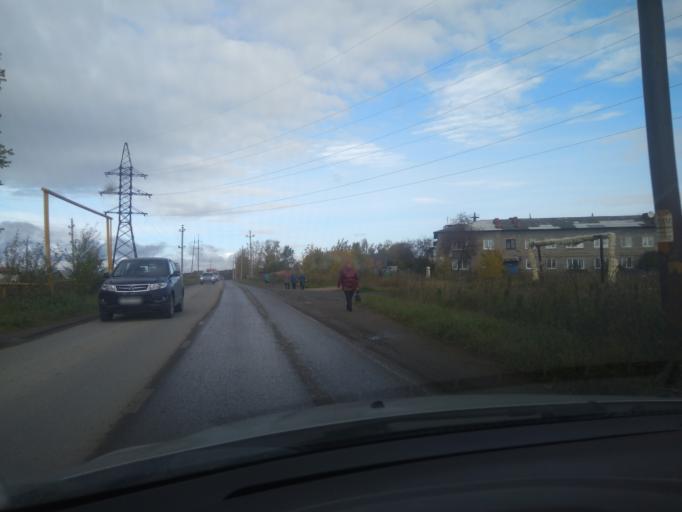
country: RU
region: Sverdlovsk
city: Nikolo-Pavlovskoye
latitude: 57.7952
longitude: 60.0537
